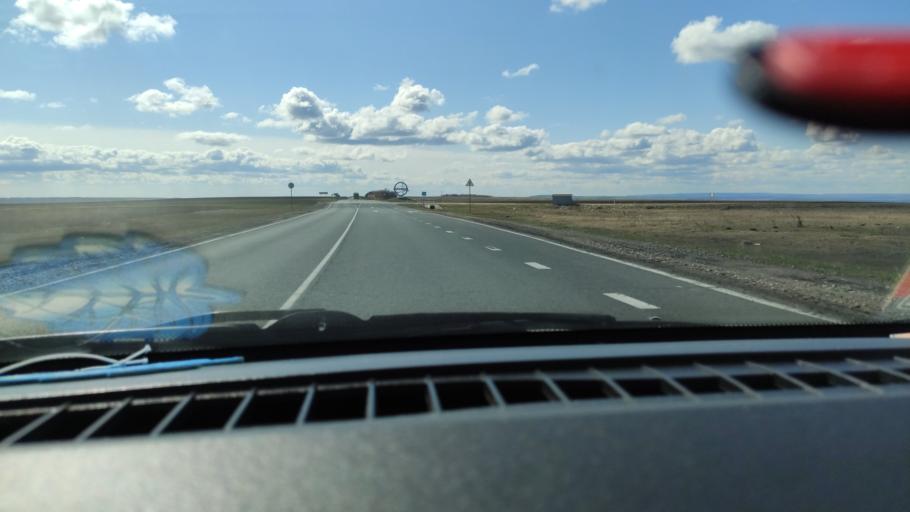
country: RU
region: Saratov
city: Dukhovnitskoye
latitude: 52.8019
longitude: 48.2299
